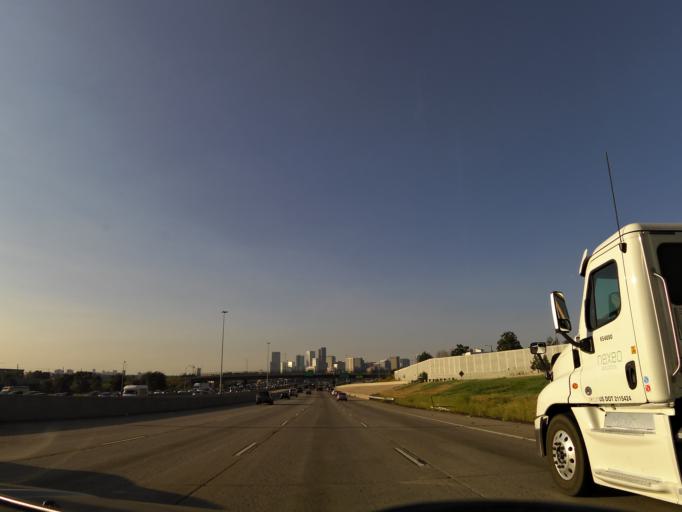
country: US
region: Colorado
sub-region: Denver County
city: Denver
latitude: 39.7791
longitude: -104.9896
